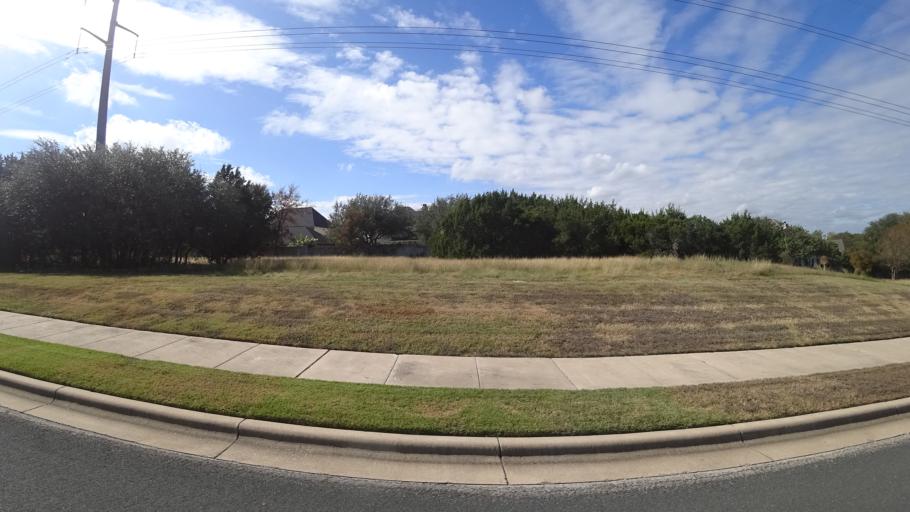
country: US
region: Texas
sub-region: Travis County
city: Hudson Bend
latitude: 30.3758
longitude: -97.8981
